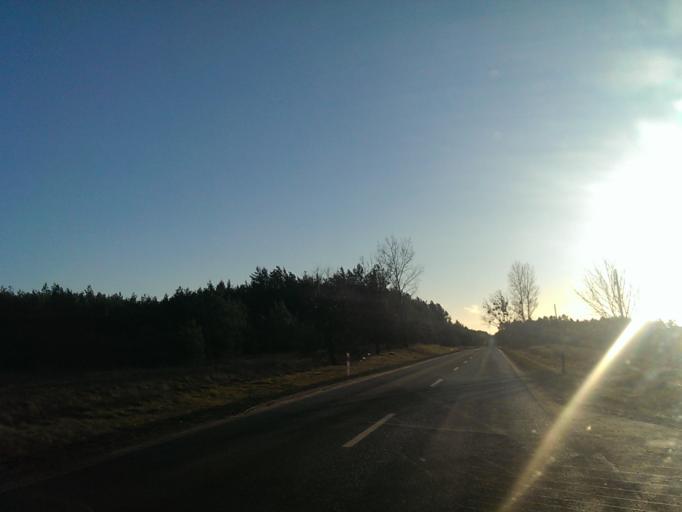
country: PL
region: Kujawsko-Pomorskie
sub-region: Powiat nakielski
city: Naklo nad Notecia
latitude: 53.0997
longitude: 17.5942
